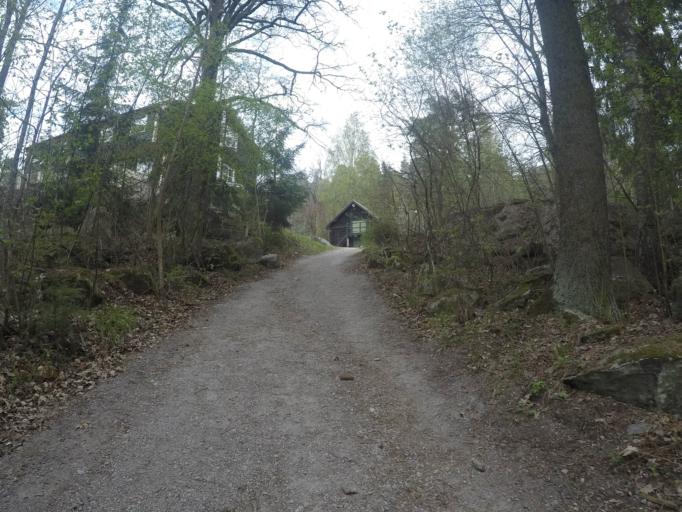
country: SE
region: Vaestmanland
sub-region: Vasteras
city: Vasteras
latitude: 59.6264
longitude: 16.5208
